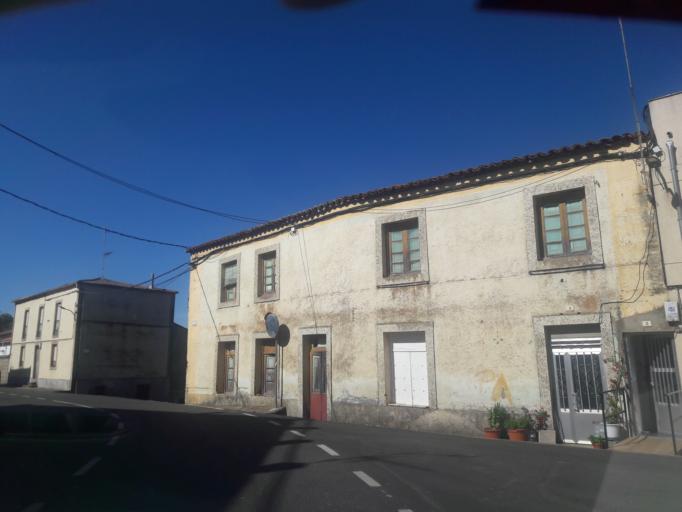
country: ES
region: Castille and Leon
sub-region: Provincia de Salamanca
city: Saucelle
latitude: 41.0461
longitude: -6.7534
